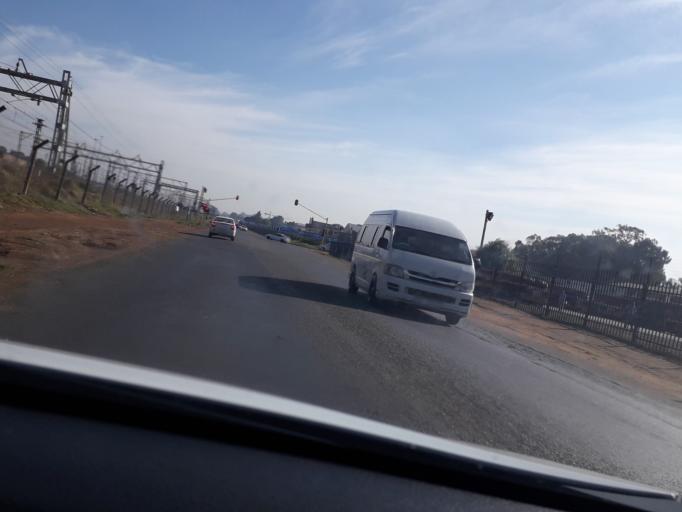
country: ZA
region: Gauteng
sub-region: Ekurhuleni Metropolitan Municipality
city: Boksburg
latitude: -26.1596
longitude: 28.2103
